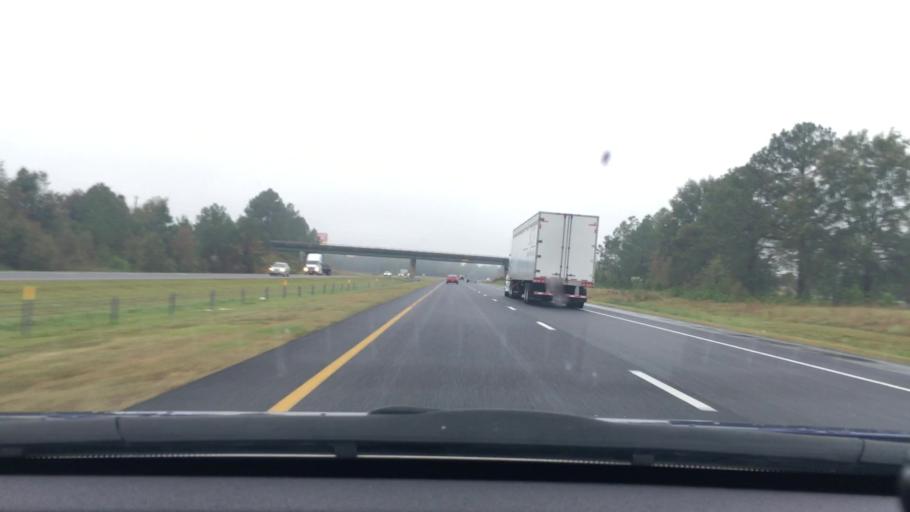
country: US
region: South Carolina
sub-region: Florence County
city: Timmonsville
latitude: 34.2011
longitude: -80.0674
